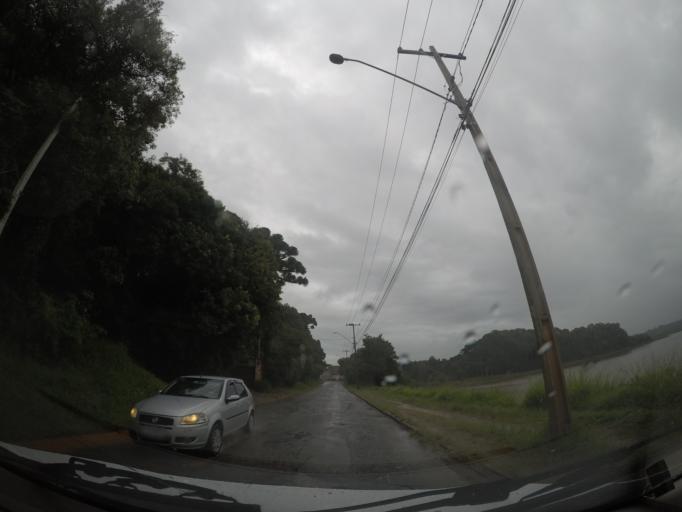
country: BR
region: Parana
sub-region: Curitiba
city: Curitiba
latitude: -25.4569
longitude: -49.3844
